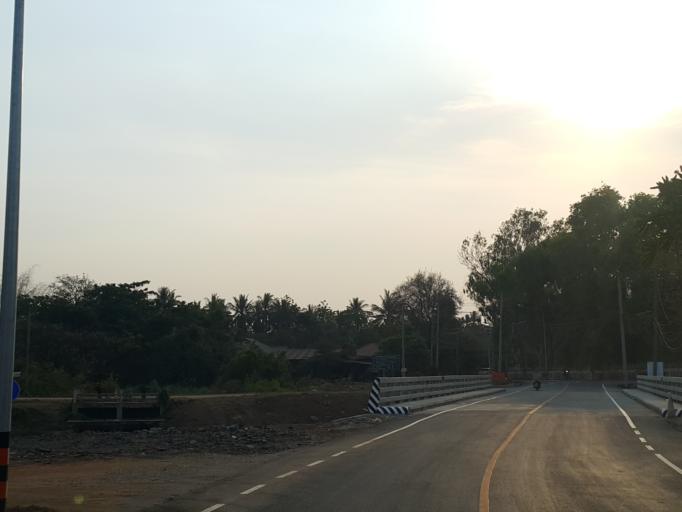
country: TH
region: Sukhothai
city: Si Samrong
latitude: 17.2182
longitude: 99.8948
